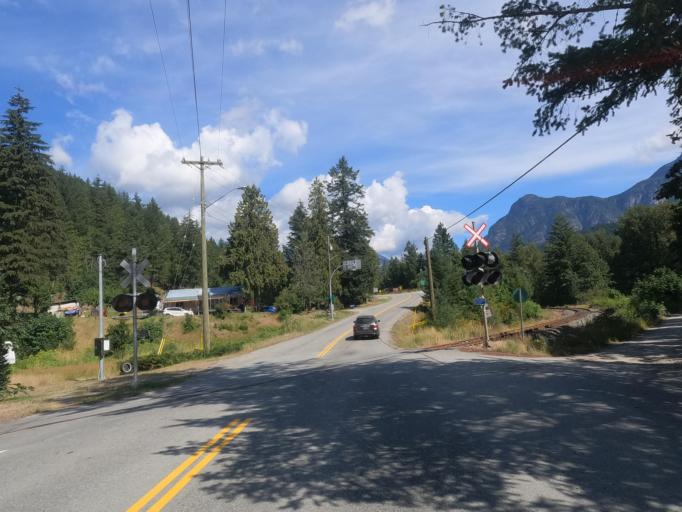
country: CA
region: British Columbia
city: Pemberton
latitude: 50.3205
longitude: -122.7208
